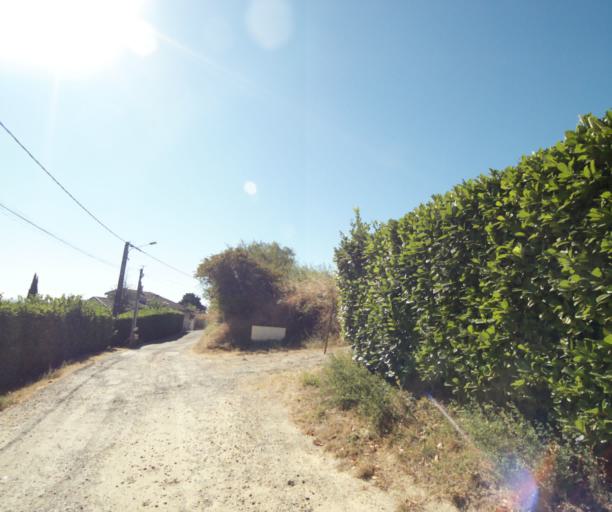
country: FR
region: Midi-Pyrenees
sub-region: Departement de la Haute-Garonne
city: Castanet-Tolosan
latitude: 43.5201
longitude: 1.4897
